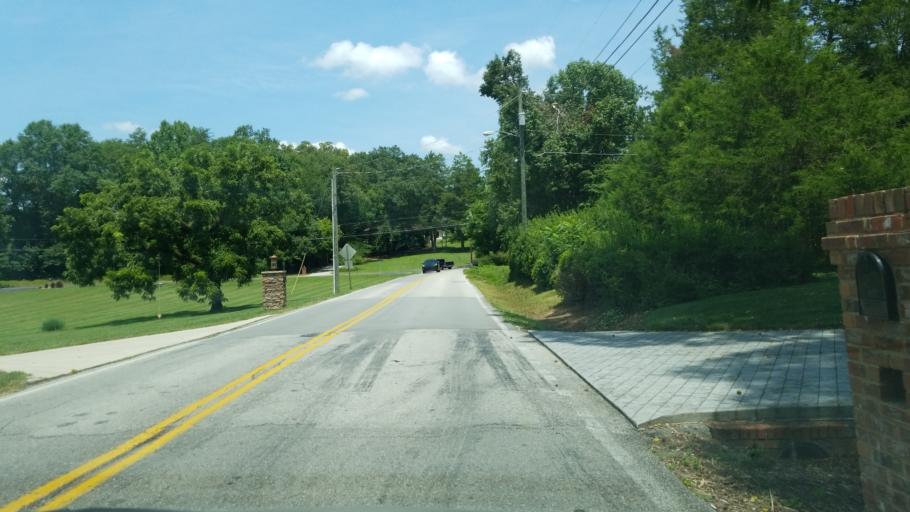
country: US
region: Tennessee
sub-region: Hamilton County
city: East Chattanooga
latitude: 35.1281
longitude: -85.2118
